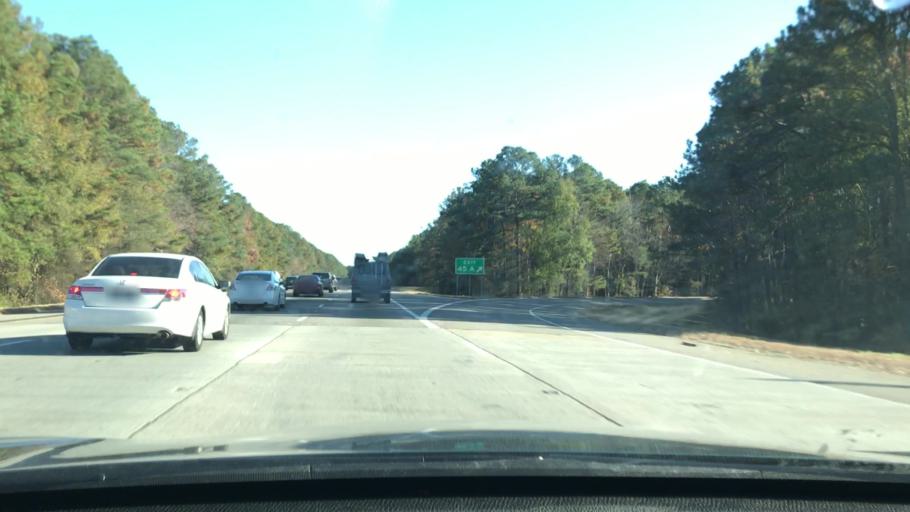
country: US
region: Virginia
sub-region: Henrico County
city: Glen Allen
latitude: 37.6666
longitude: -77.4843
